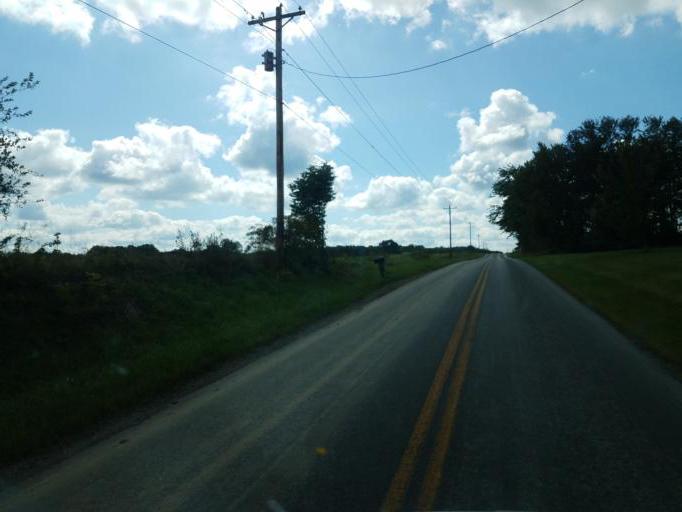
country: US
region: Ohio
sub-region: Wayne County
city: West Salem
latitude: 41.0173
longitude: -82.1265
